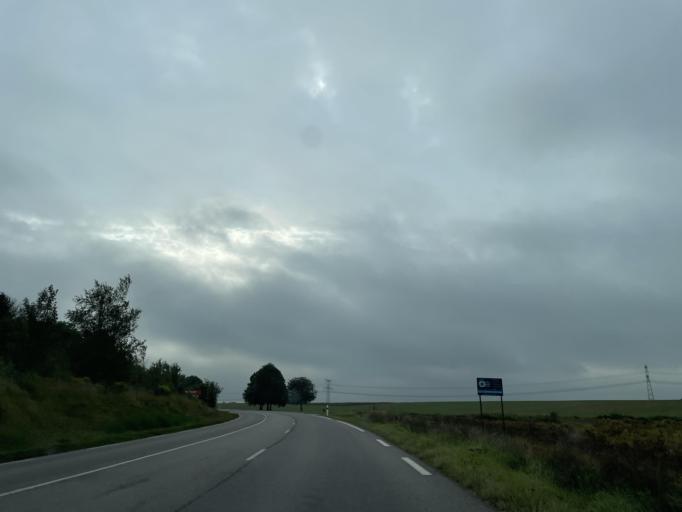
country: FR
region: Haute-Normandie
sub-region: Departement de la Seine-Maritime
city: Criel-sur-Mer
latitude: 50.0199
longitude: 1.3506
